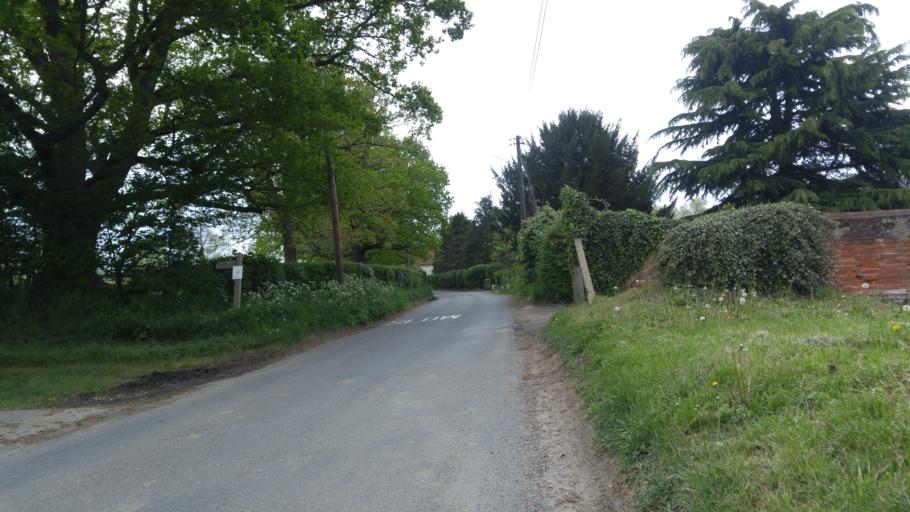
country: GB
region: England
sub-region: Suffolk
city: Sudbury
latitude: 51.9893
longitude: 0.7515
